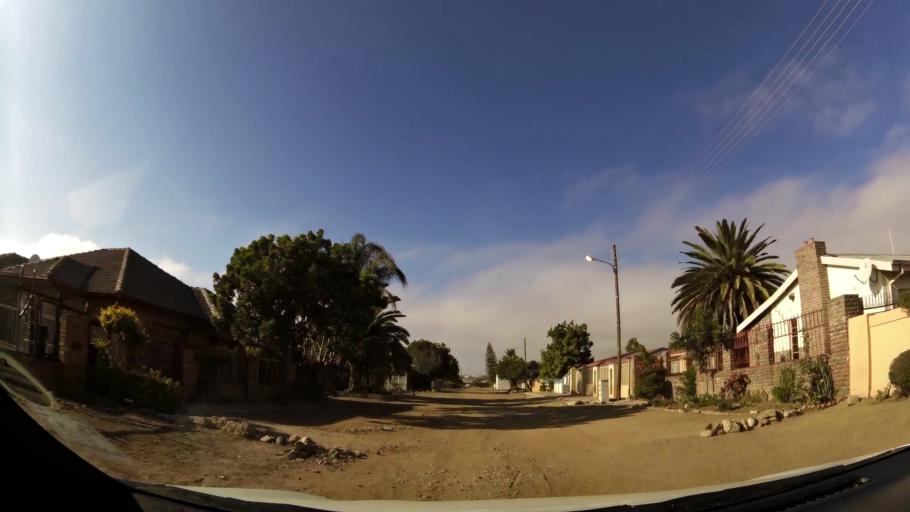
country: ZA
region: Limpopo
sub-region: Capricorn District Municipality
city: Polokwane
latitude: -23.8470
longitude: 29.3885
